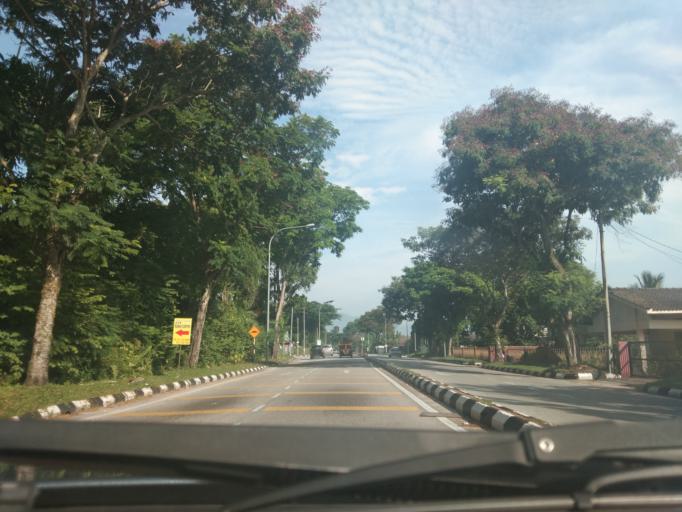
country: MY
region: Perak
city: Ipoh
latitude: 4.5676
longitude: 101.1202
